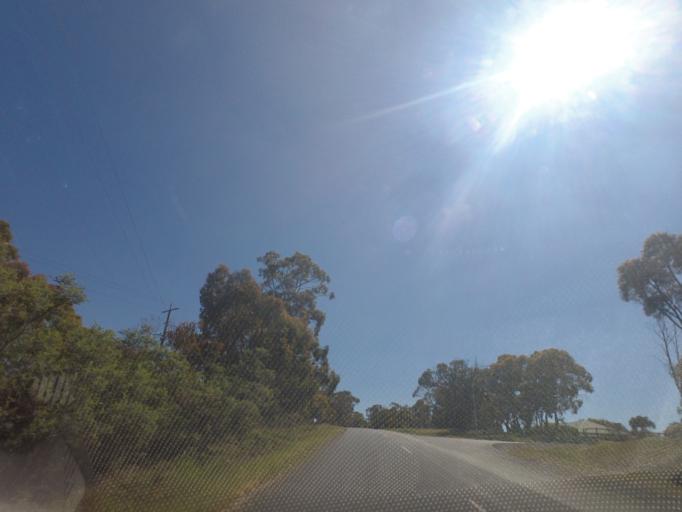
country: AU
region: Victoria
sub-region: Whittlesea
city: Whittlesea
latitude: -37.3991
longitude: 144.9543
